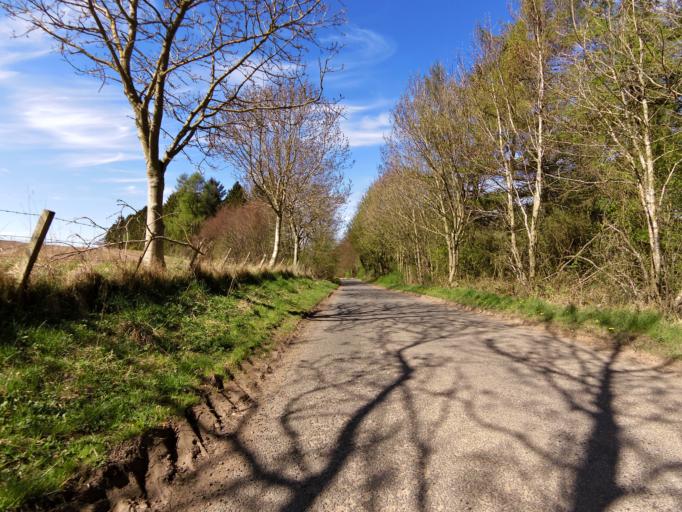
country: GB
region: Scotland
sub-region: Fife
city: Cupar
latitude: 56.3870
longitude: -3.0773
